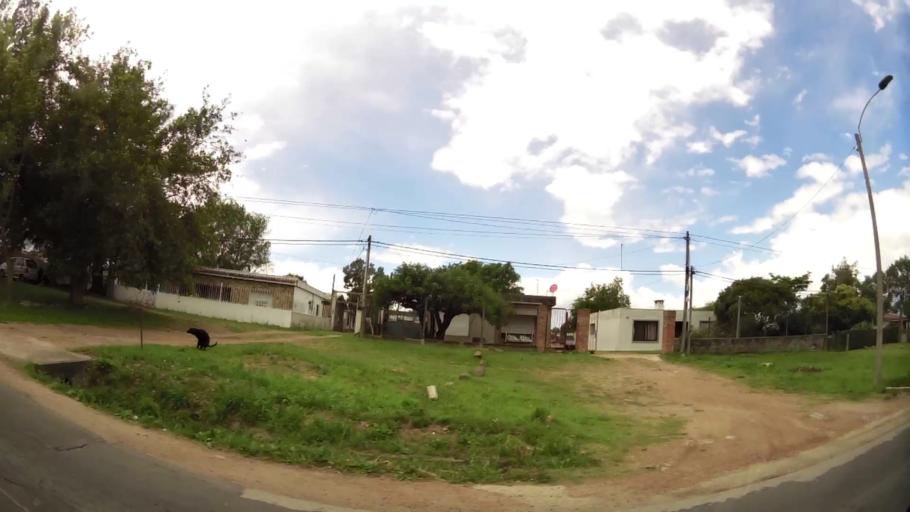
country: UY
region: Canelones
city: La Paz
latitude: -34.8075
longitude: -56.1631
